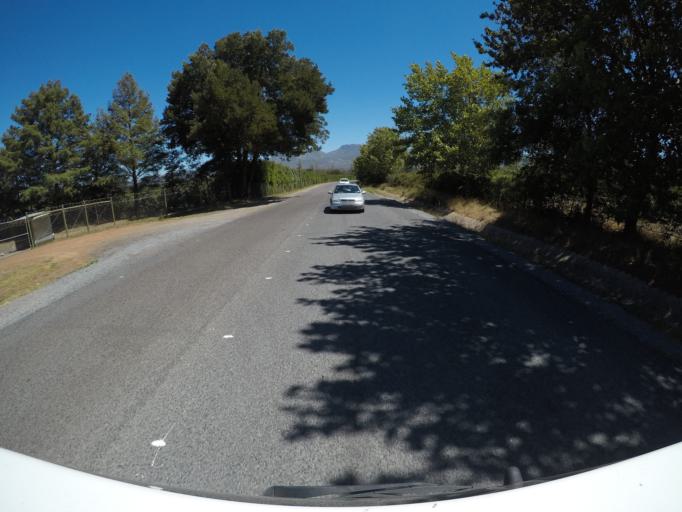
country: ZA
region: Western Cape
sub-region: Overberg District Municipality
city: Grabouw
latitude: -34.1783
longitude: 19.0356
